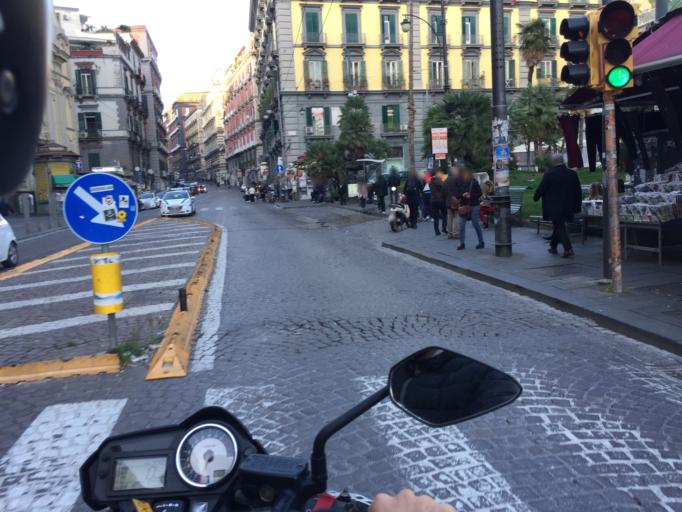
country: IT
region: Campania
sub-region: Provincia di Napoli
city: Napoli
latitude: 40.8495
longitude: 14.2499
